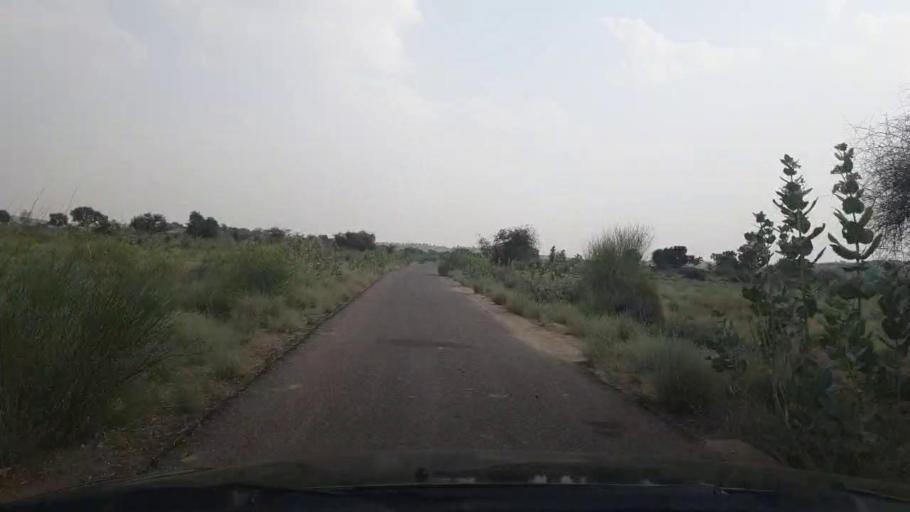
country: PK
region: Sindh
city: Islamkot
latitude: 25.0097
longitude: 70.5962
